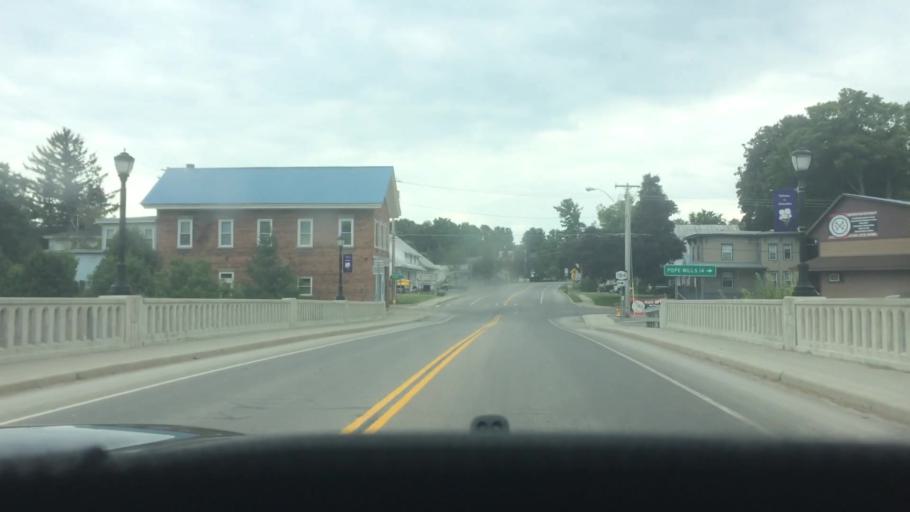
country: US
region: New York
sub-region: St. Lawrence County
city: Ogdensburg
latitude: 44.6169
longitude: -75.4054
